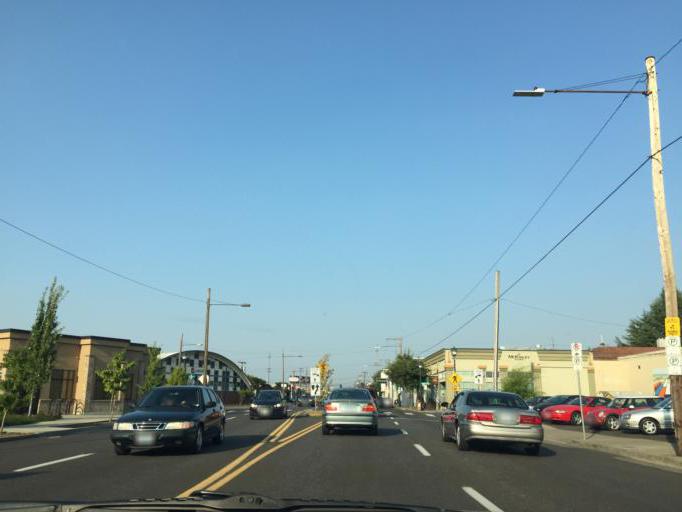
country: US
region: Oregon
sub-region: Multnomah County
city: Portland
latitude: 45.5280
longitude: -122.6401
